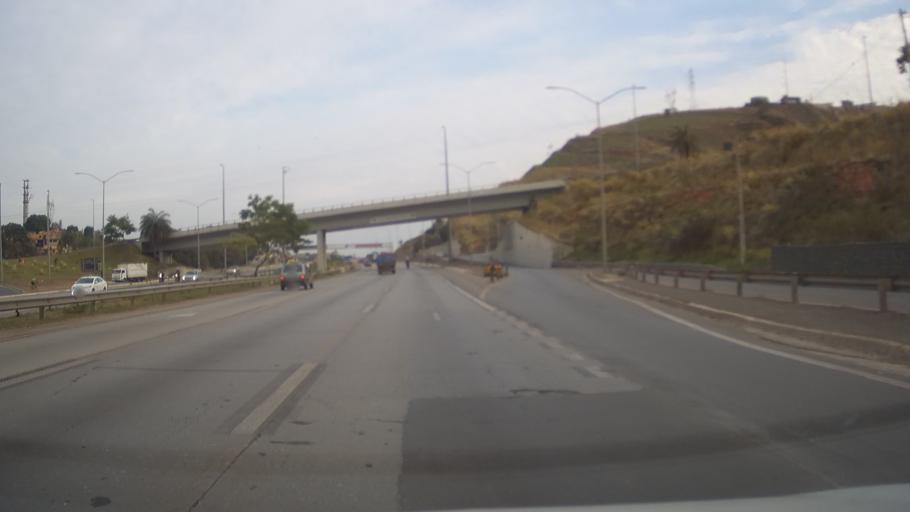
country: BR
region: Minas Gerais
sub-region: Vespasiano
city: Vespasiano
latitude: -19.7809
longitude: -43.9485
